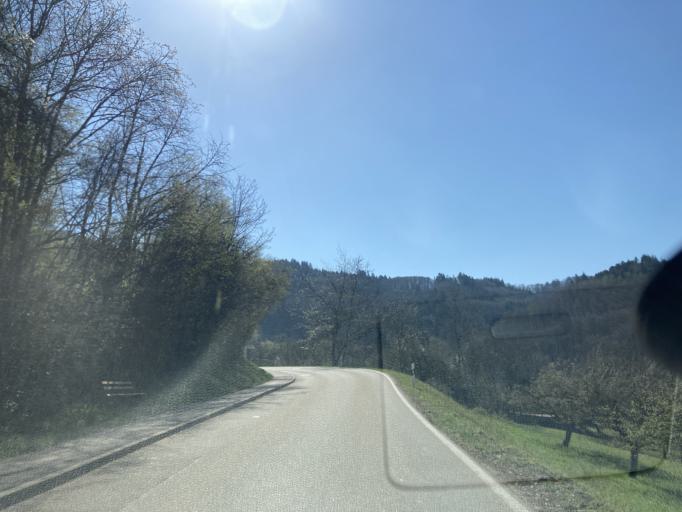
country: DE
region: Baden-Wuerttemberg
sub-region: Freiburg Region
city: Badenweiler
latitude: 47.7824
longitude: 7.6707
